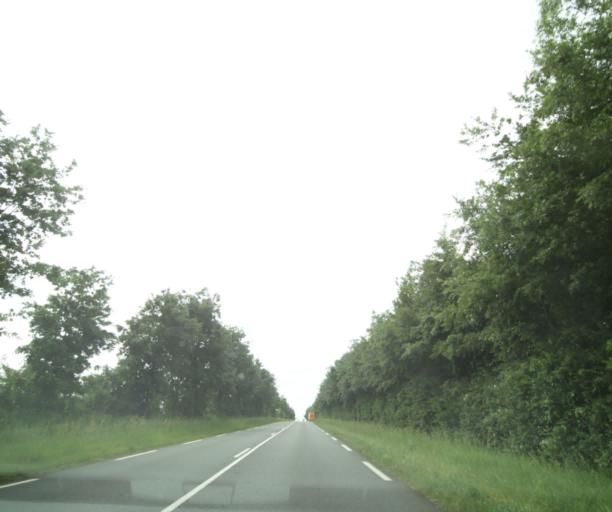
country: FR
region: Pays de la Loire
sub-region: Departement de Maine-et-Loire
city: Montreuil-Bellay
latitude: 47.1617
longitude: -0.1433
